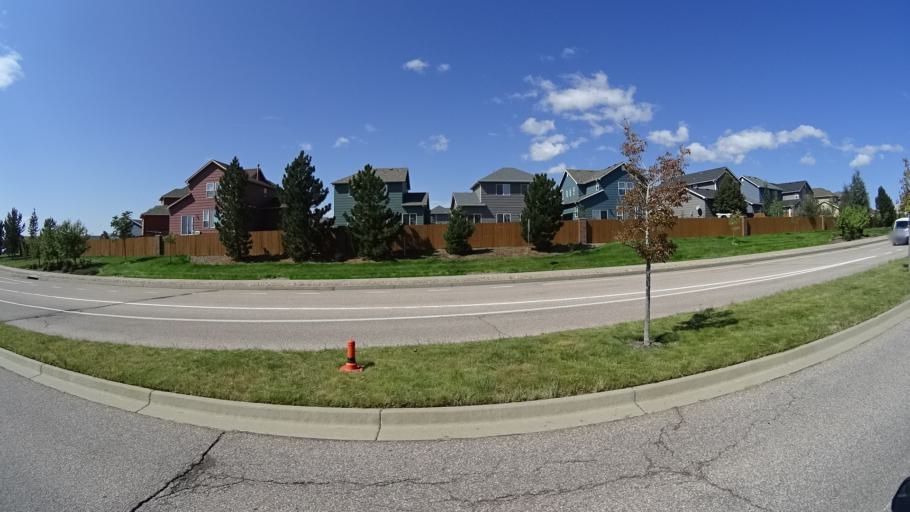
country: US
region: Colorado
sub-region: El Paso County
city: Cimarron Hills
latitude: 38.9270
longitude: -104.6994
